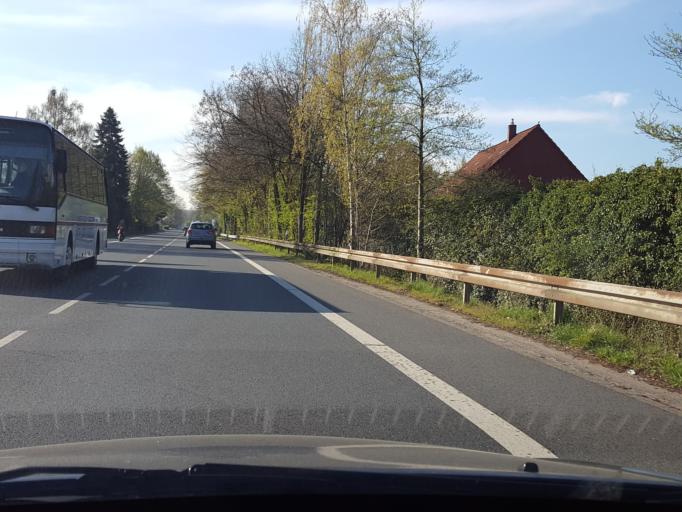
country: DE
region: North Rhine-Westphalia
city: Datteln
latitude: 51.6638
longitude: 7.3485
